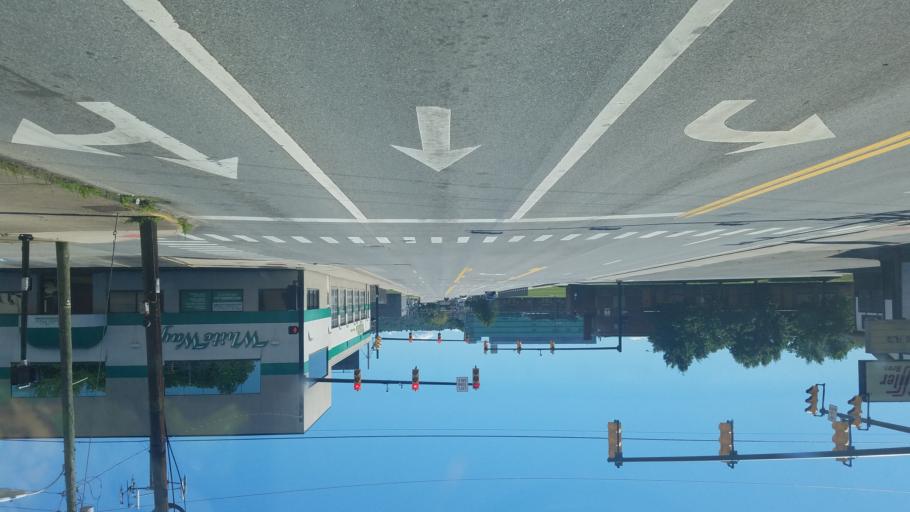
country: US
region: West Virginia
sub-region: Cabell County
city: Huntington
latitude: 38.4147
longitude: -82.4296
